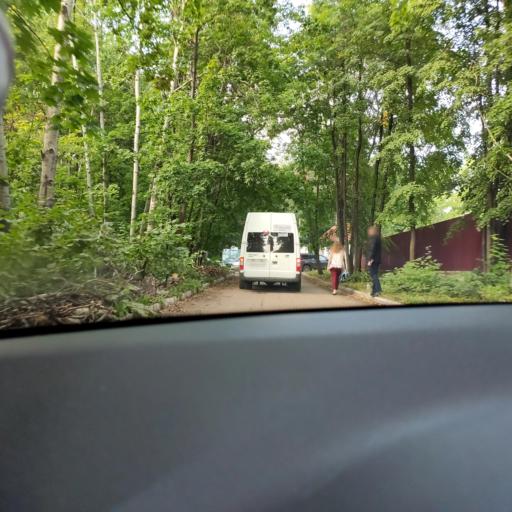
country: RU
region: Samara
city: Novosemeykino
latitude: 53.3510
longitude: 50.2442
